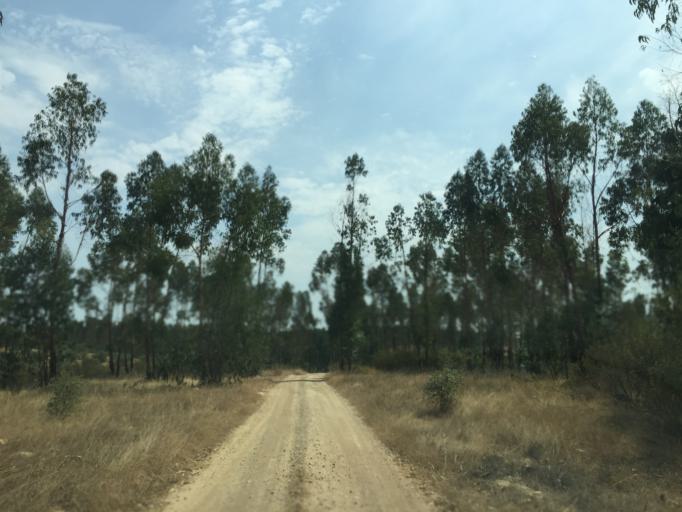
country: PT
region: Setubal
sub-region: Grandola
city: Grandola
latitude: 38.0637
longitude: -8.4426
